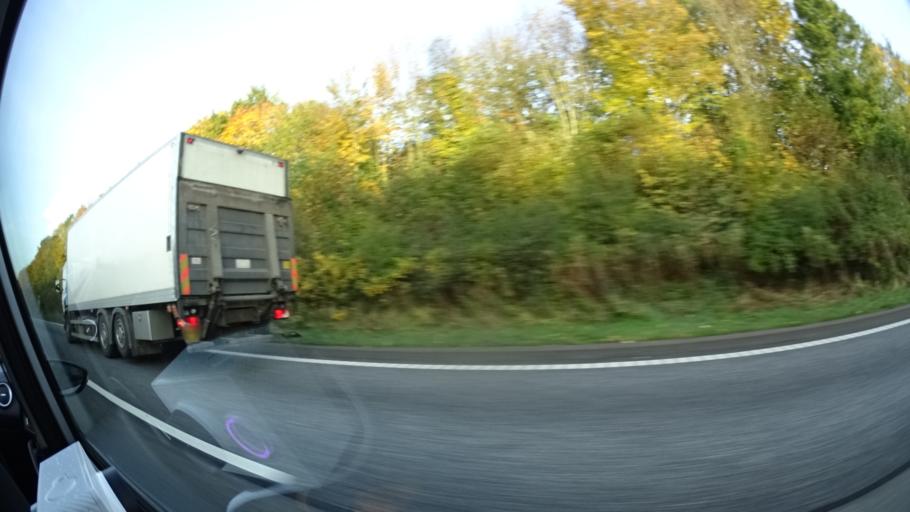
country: DK
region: Central Jutland
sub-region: Skanderborg Kommune
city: Skanderborg
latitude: 56.0474
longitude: 9.9131
